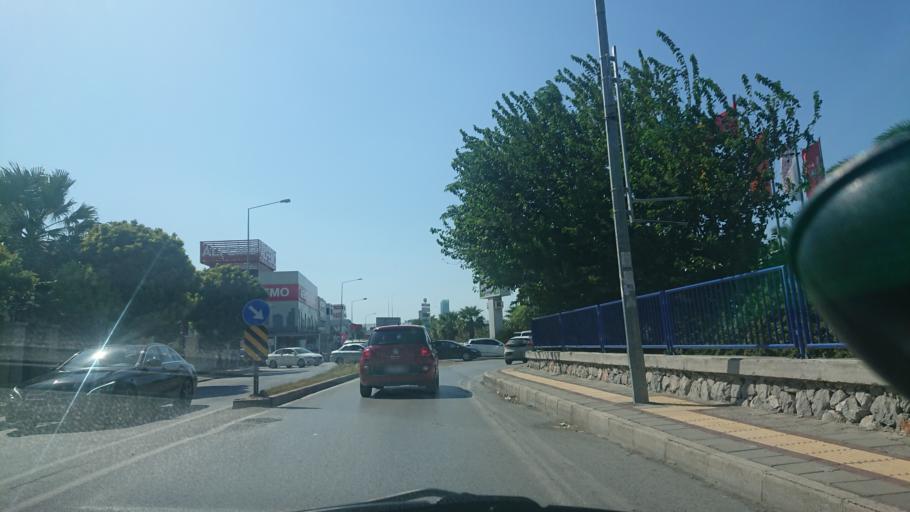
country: TR
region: Izmir
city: Bornova
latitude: 38.4488
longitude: 27.2099
